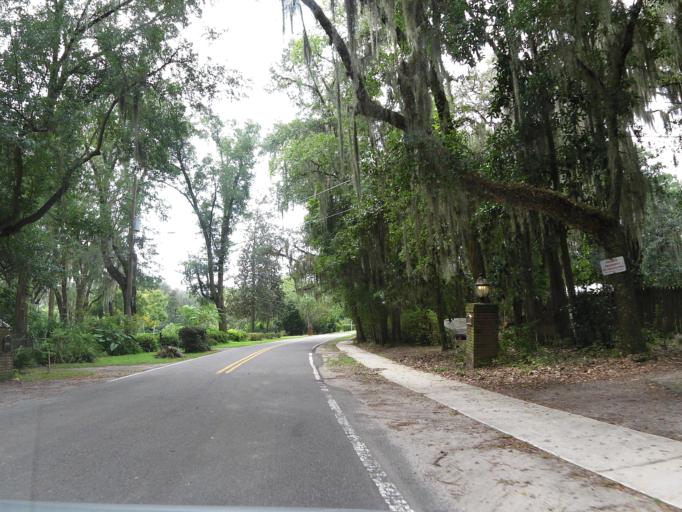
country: US
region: Florida
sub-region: Clay County
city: Bellair-Meadowbrook Terrace
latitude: 30.2582
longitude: -81.7208
